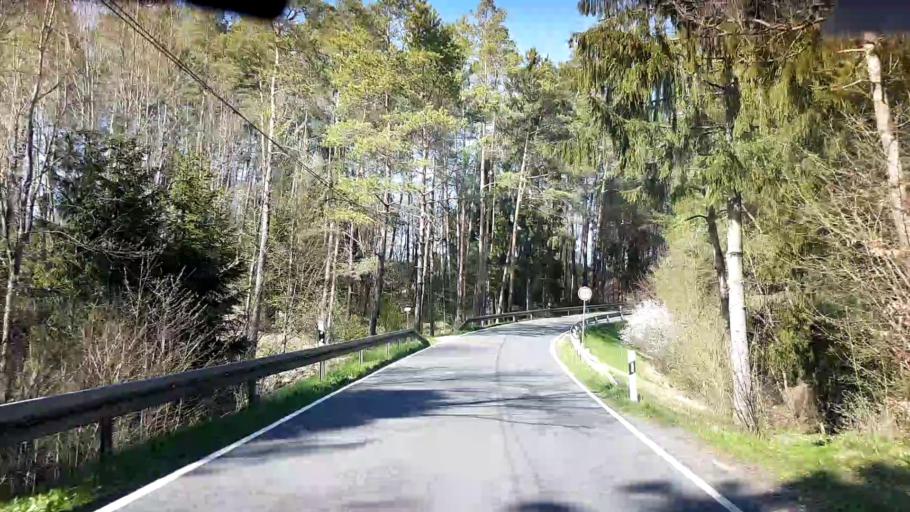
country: DE
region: Bavaria
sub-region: Upper Franconia
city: Pottenstein
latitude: 49.7961
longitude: 11.3768
